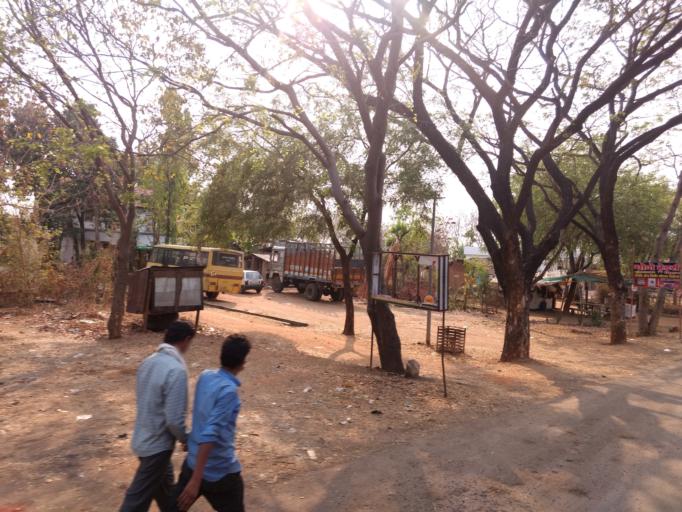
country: IN
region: Maharashtra
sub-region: Bhandara
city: Pauni
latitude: 20.7454
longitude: 79.5456
